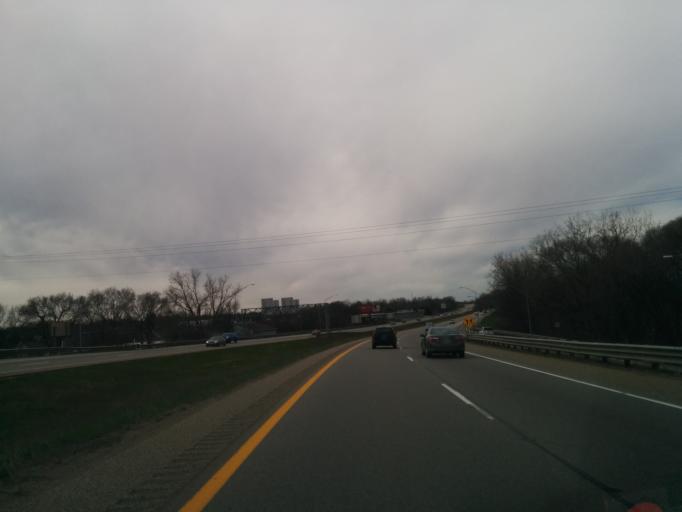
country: US
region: Michigan
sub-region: Kent County
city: Grandville
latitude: 42.9139
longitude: -85.7659
